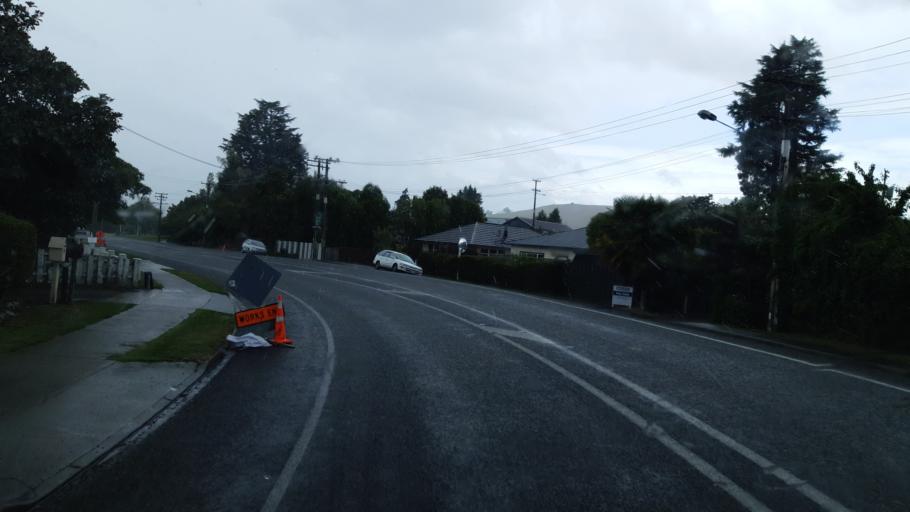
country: NZ
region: Tasman
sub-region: Tasman District
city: Wakefield
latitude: -41.4045
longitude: 173.0497
